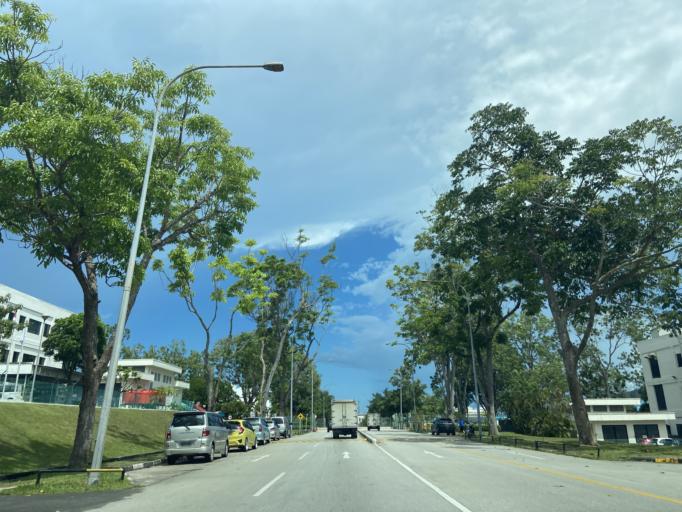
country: SG
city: Singapore
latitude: 1.0654
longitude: 104.0306
